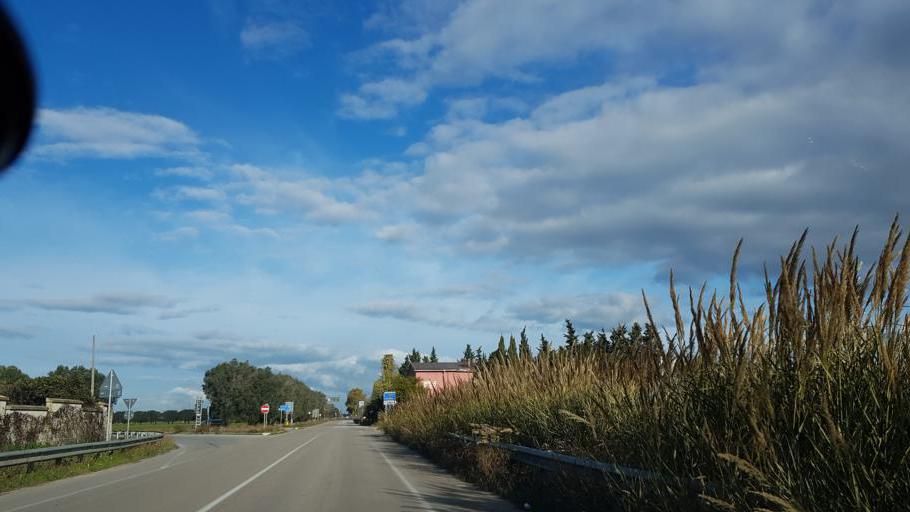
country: IT
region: Apulia
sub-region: Provincia di Brindisi
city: Tuturano
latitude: 40.5495
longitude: 17.9761
